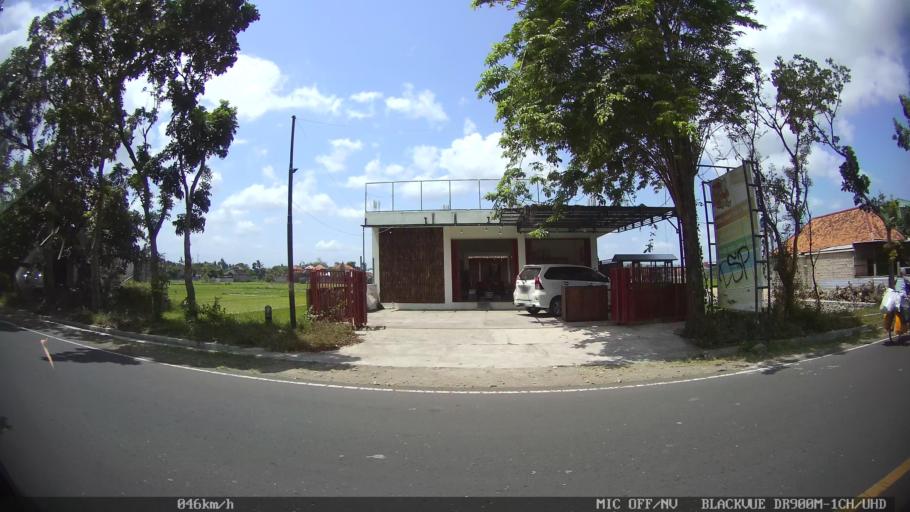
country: ID
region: Daerah Istimewa Yogyakarta
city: Bantul
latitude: -7.9001
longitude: 110.3460
